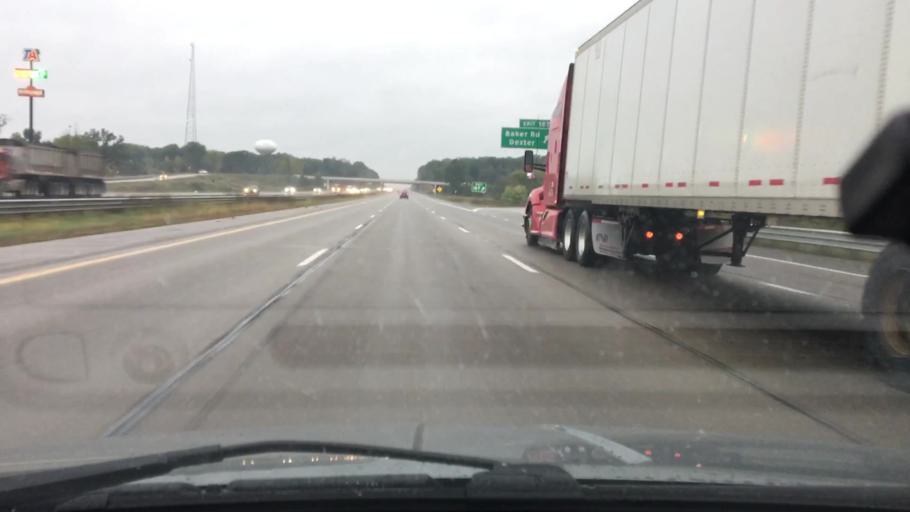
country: US
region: Michigan
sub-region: Washtenaw County
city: Dexter
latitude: 42.2989
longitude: -83.8718
